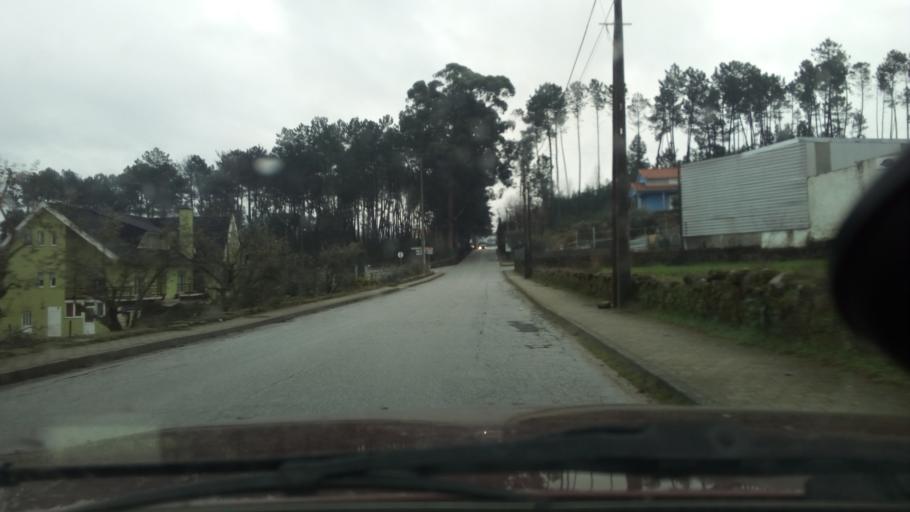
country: PT
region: Viseu
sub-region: Mangualde
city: Mangualde
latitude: 40.6256
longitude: -7.8065
